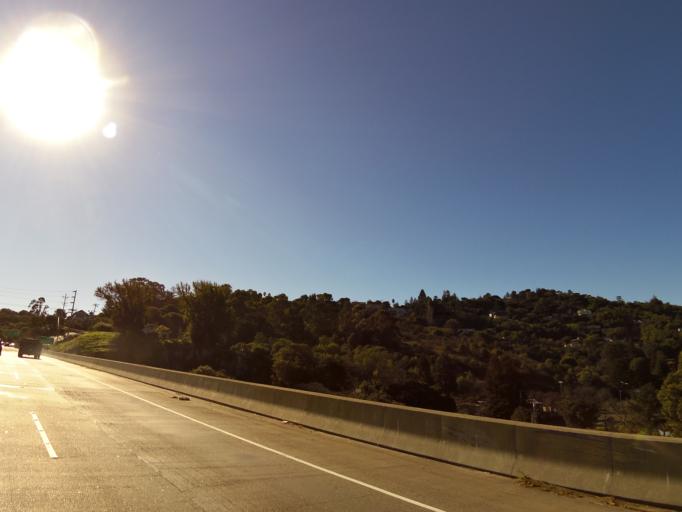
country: US
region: California
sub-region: Marin County
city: San Rafael
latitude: 37.9580
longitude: -122.5093
